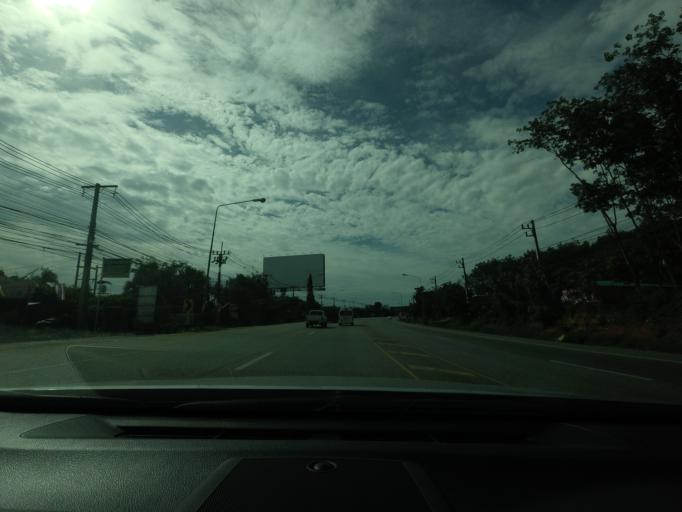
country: TH
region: Songkhla
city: Hat Yai
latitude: 6.9790
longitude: 100.4263
